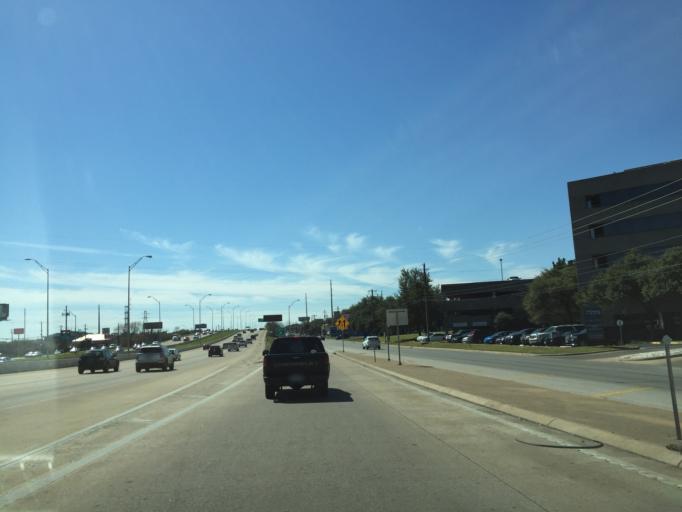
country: US
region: Texas
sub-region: Williamson County
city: Jollyville
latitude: 30.4053
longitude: -97.7457
